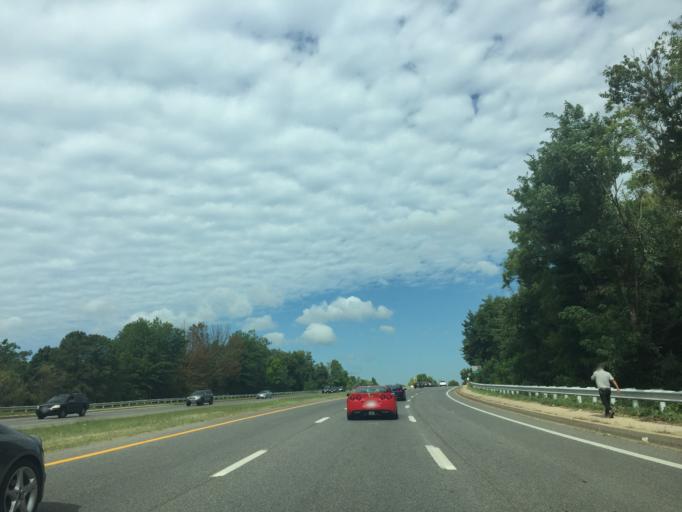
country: US
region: Maryland
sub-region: Prince George's County
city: Laurel
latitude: 39.0959
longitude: -76.8438
